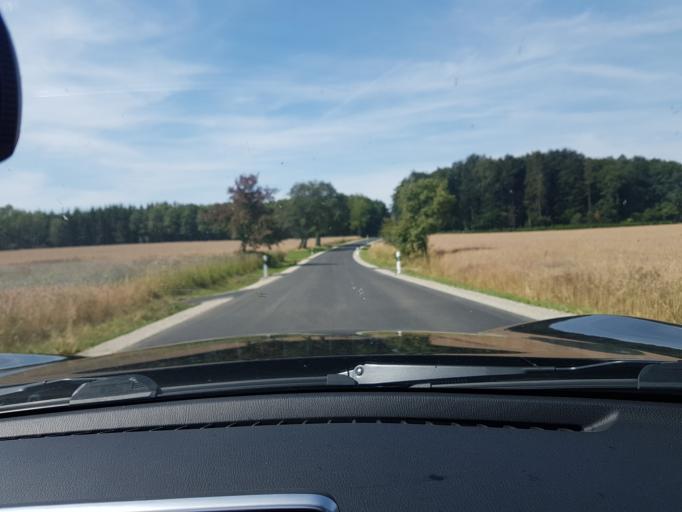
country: DE
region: Baden-Wuerttemberg
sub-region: Karlsruhe Region
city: Limbach
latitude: 49.4549
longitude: 9.2025
